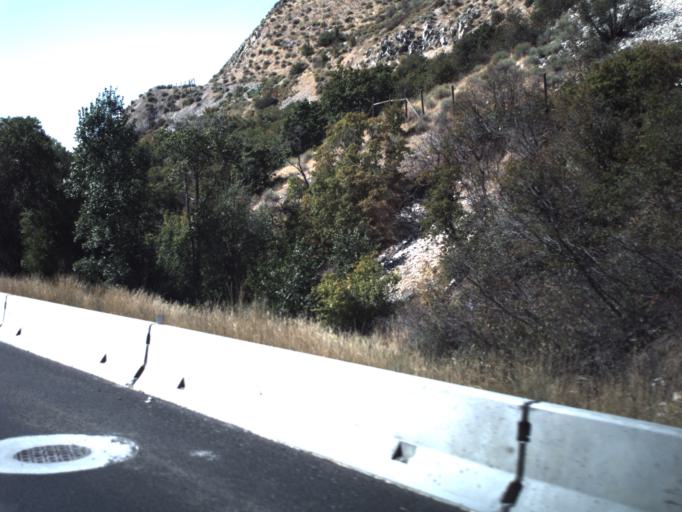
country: US
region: Utah
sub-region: Box Elder County
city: Brigham City
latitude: 41.4961
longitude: -111.9608
